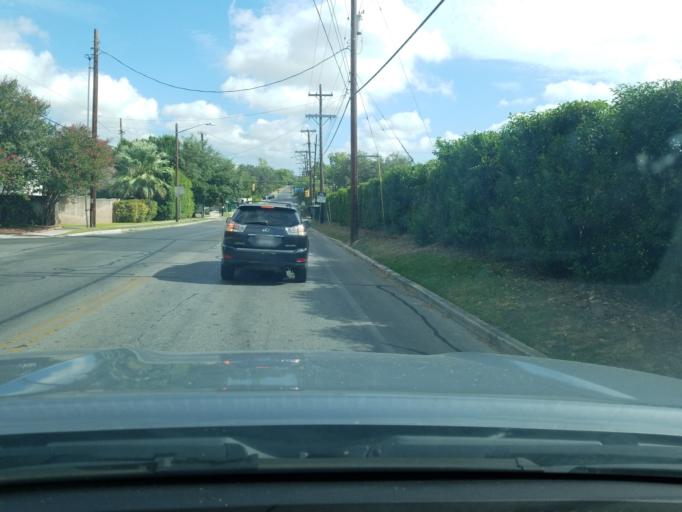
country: US
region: Texas
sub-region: Bexar County
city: Terrell Hills
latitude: 29.4674
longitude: -98.4607
